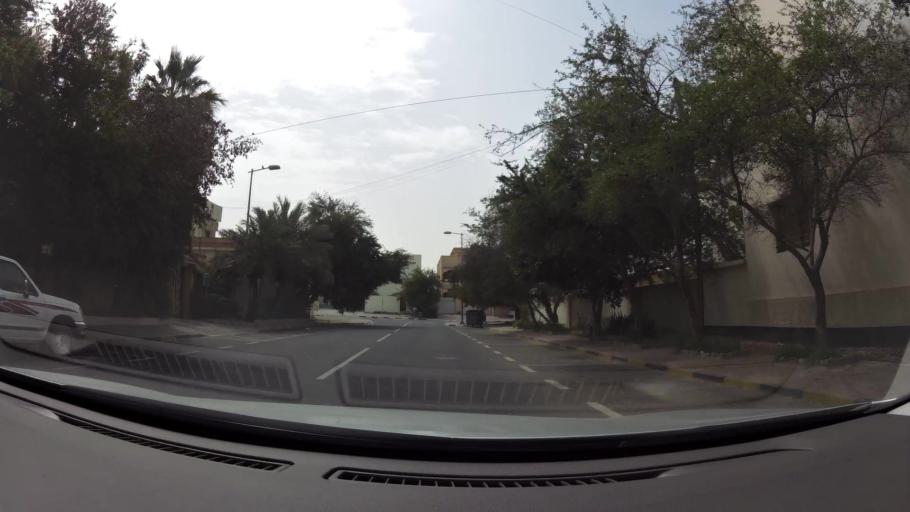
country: QA
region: Baladiyat ar Rayyan
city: Ar Rayyan
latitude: 25.3109
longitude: 51.4743
